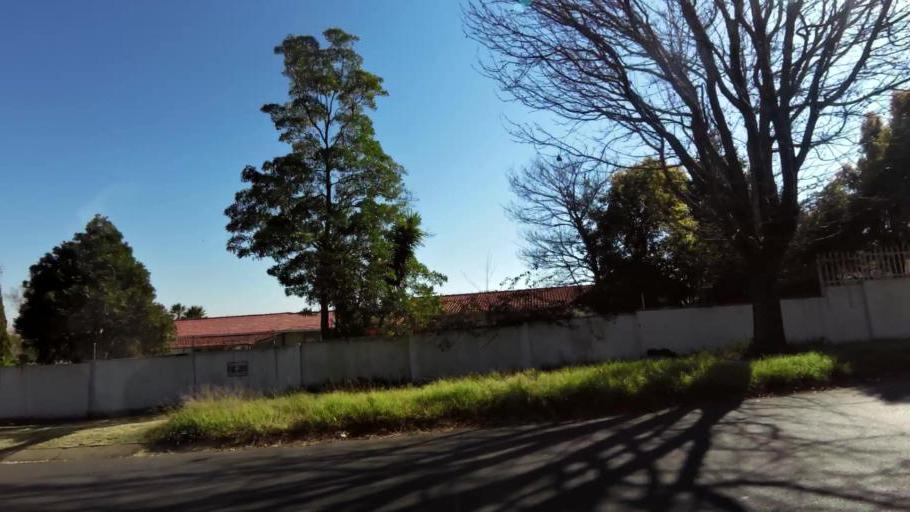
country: ZA
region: Gauteng
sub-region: City of Johannesburg Metropolitan Municipality
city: Johannesburg
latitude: -26.2468
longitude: 27.9944
